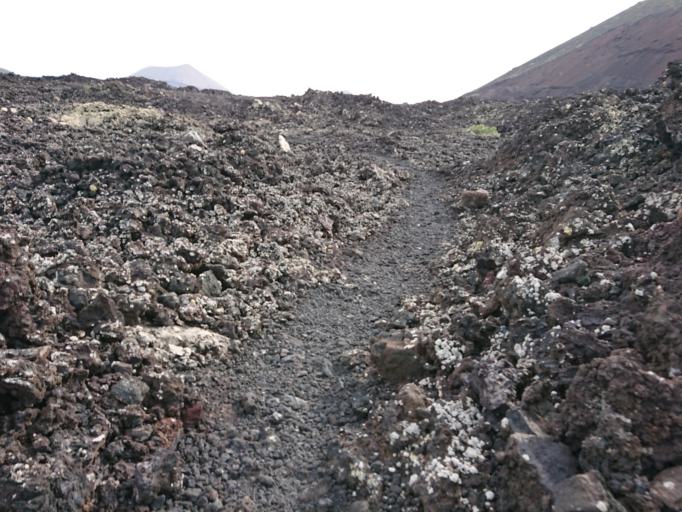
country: ES
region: Canary Islands
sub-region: Provincia de Las Palmas
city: Tinajo
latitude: 29.0116
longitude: -13.6774
